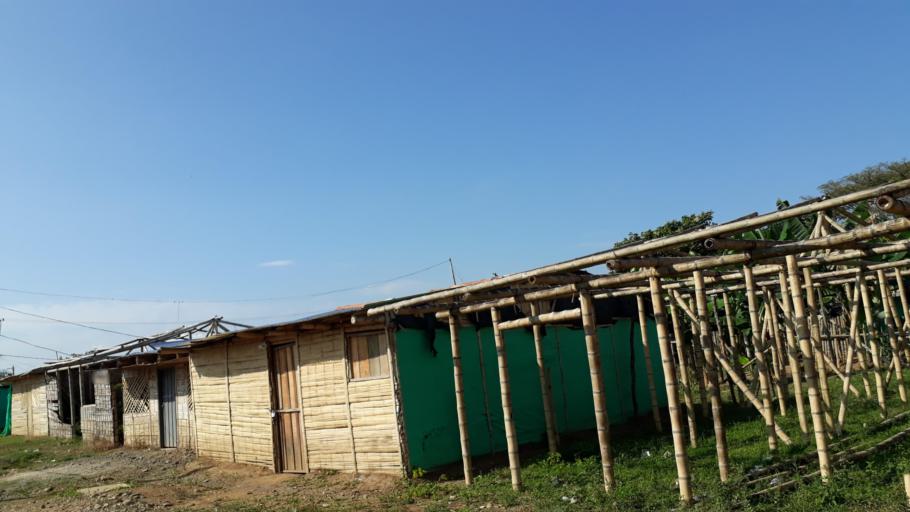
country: CO
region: Cauca
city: Buenos Aires
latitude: 3.1262
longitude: -76.6240
